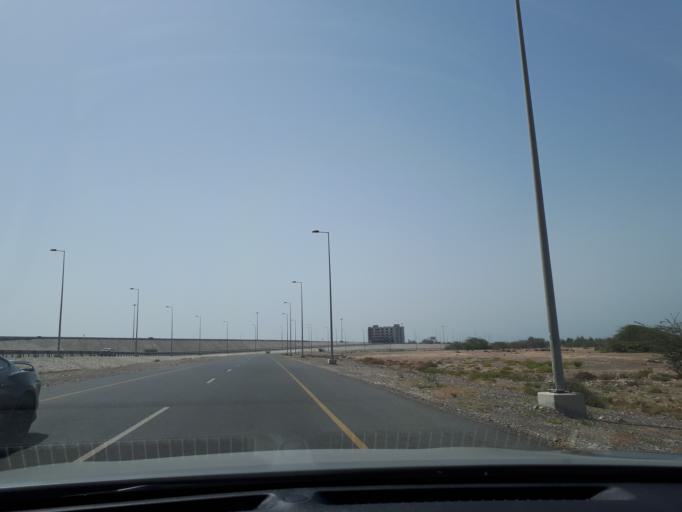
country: OM
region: Al Batinah
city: Barka'
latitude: 23.6882
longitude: 58.0268
